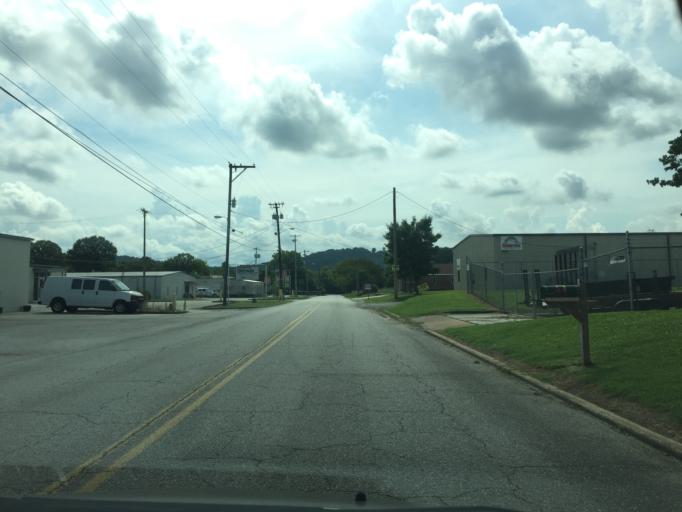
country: US
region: Tennessee
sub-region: Hamilton County
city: East Chattanooga
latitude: 35.0698
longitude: -85.2662
